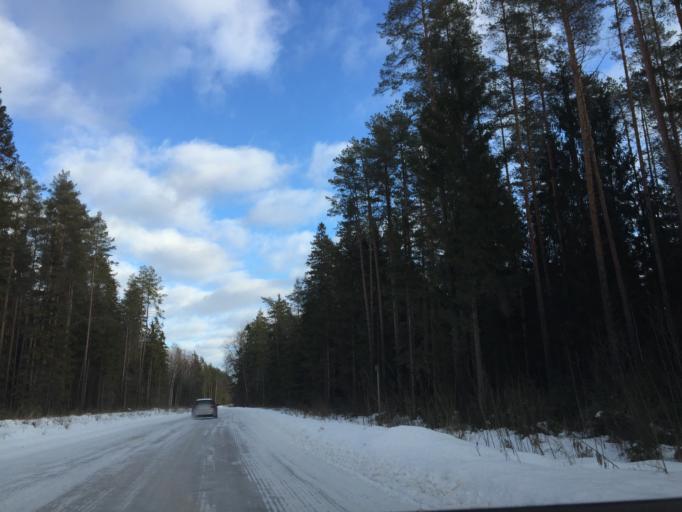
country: LV
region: Ogre
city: Jumprava
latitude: 56.5846
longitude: 24.9612
